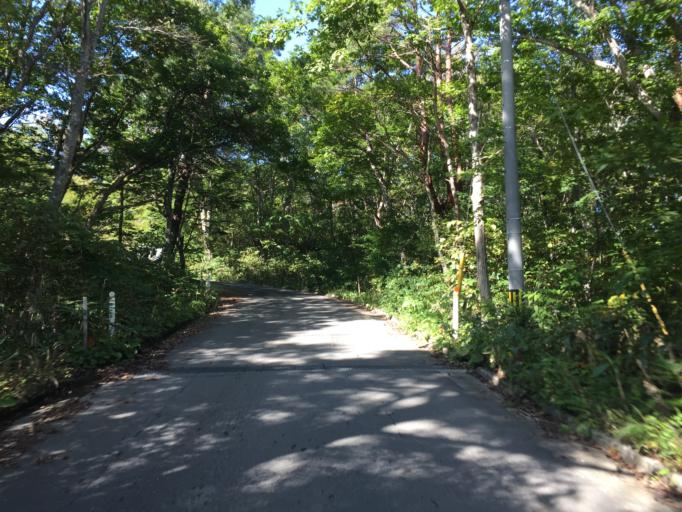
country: JP
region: Yamagata
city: Yonezawa
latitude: 37.8099
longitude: 140.2545
